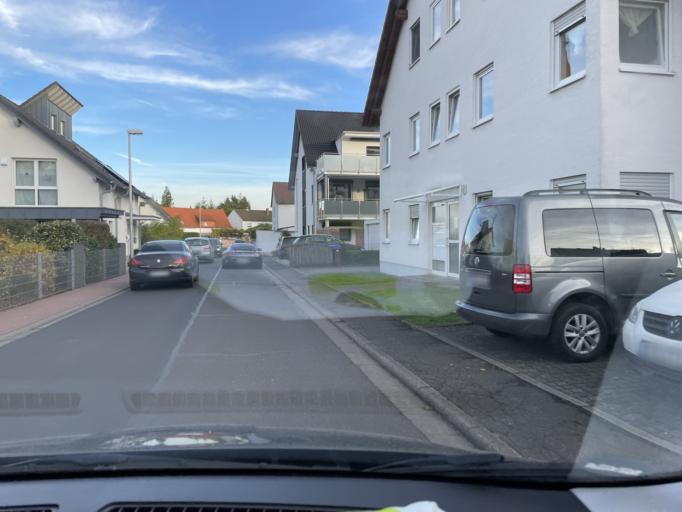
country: DE
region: Bavaria
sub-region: Regierungsbezirk Unterfranken
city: Grossostheim
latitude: 49.9251
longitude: 9.0710
